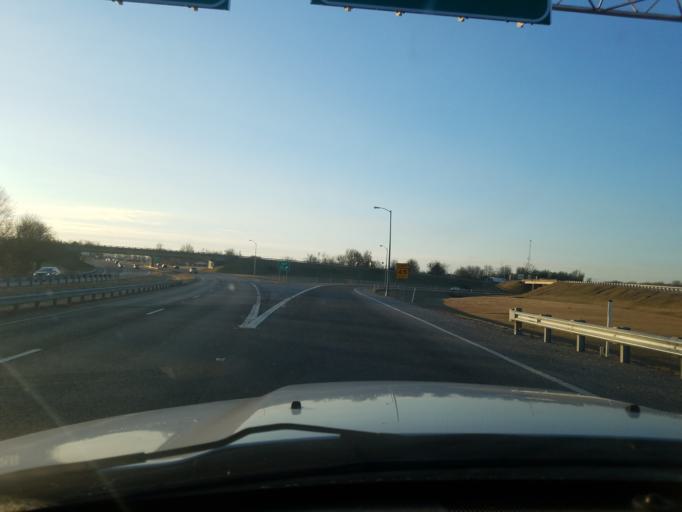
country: US
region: Kentucky
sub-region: Henderson County
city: Henderson
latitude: 37.8272
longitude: -87.5670
